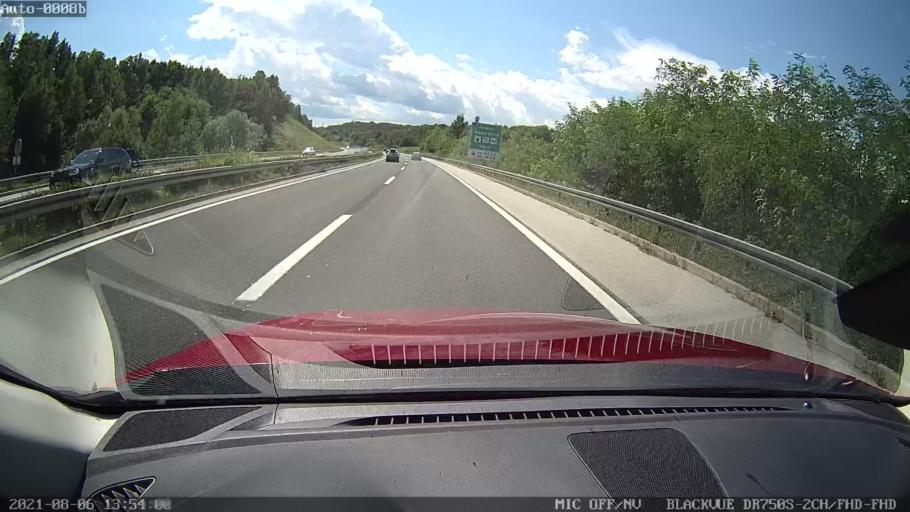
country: HR
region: Karlovacka
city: Ozalj
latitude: 45.4606
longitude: 15.3813
